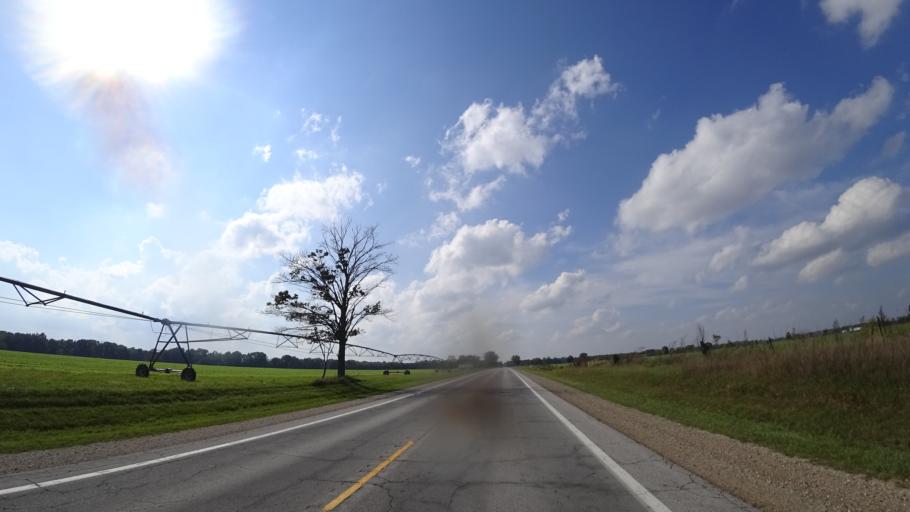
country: US
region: Michigan
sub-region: Saint Joseph County
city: Colon
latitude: 42.0102
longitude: -85.3921
